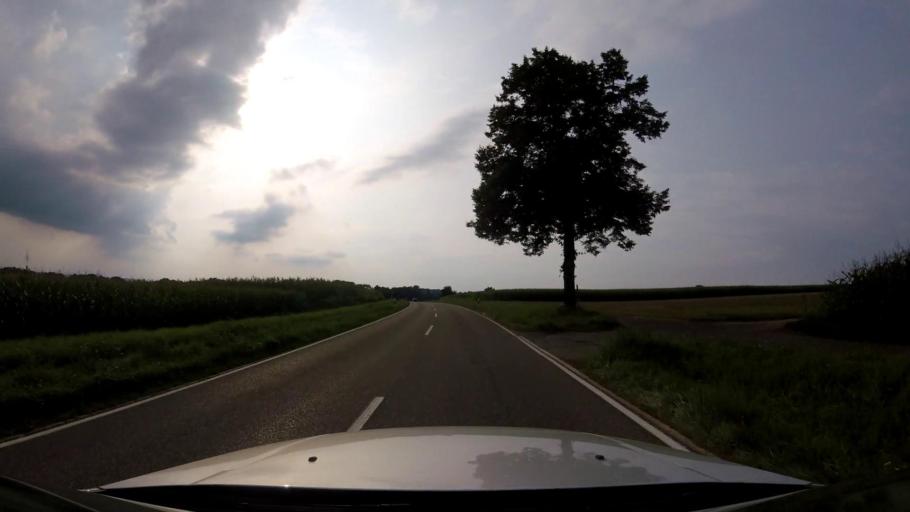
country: DE
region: Baden-Wuerttemberg
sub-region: Regierungsbezirk Stuttgart
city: Mutlangen
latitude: 48.8376
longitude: 9.7800
